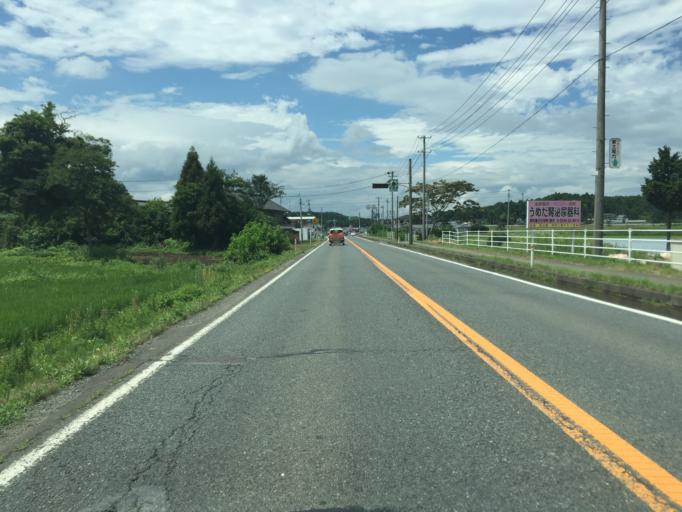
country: JP
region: Fukushima
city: Namie
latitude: 37.7158
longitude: 140.9598
